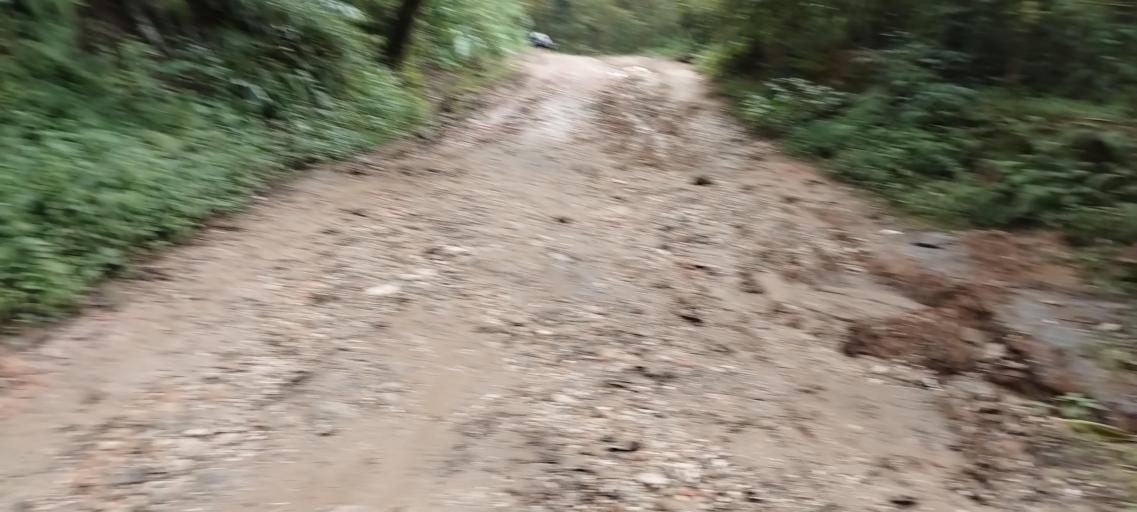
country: NP
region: Central Region
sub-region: Bagmati Zone
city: Kathmandu
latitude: 27.7905
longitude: 85.3728
